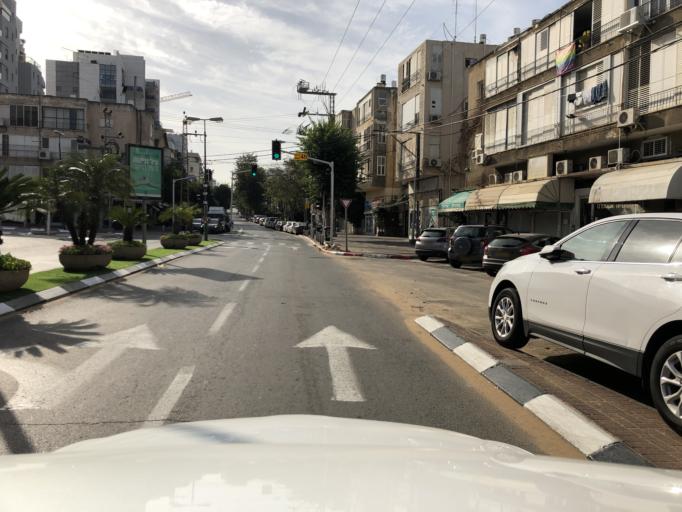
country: IL
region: Tel Aviv
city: Bene Beraq
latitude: 32.0788
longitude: 34.8253
